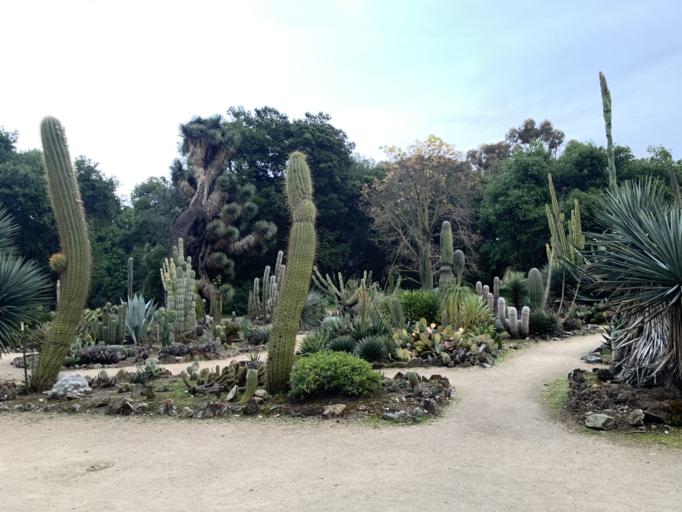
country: US
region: California
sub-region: Santa Clara County
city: Stanford
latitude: 37.4357
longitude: -122.1712
